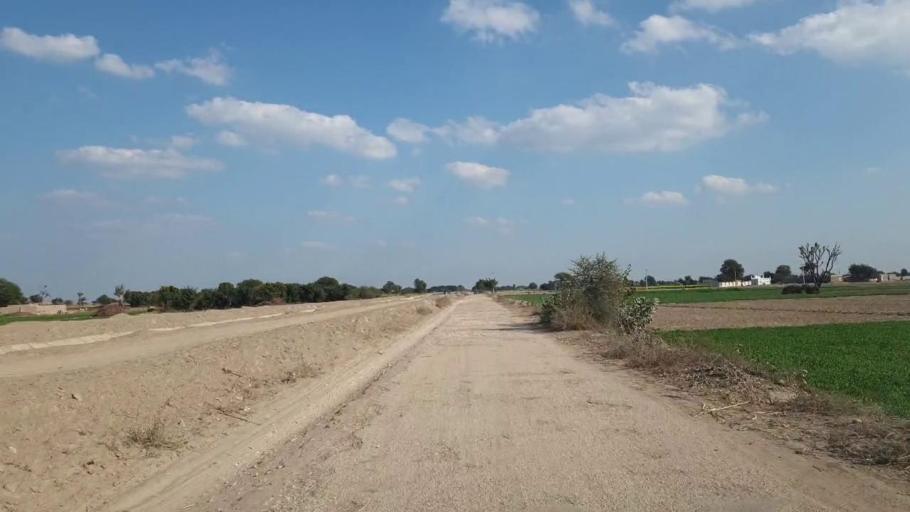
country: PK
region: Sindh
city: Shahpur Chakar
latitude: 26.1059
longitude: 68.5797
